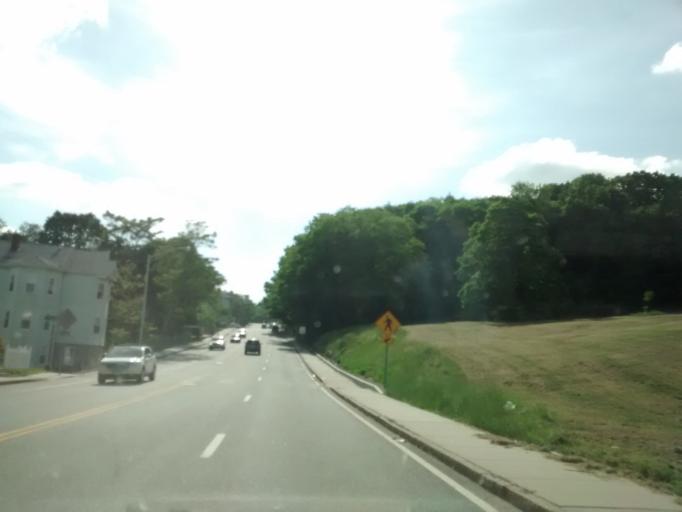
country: US
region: Massachusetts
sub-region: Worcester County
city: Hamilton
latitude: 42.2736
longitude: -71.7757
